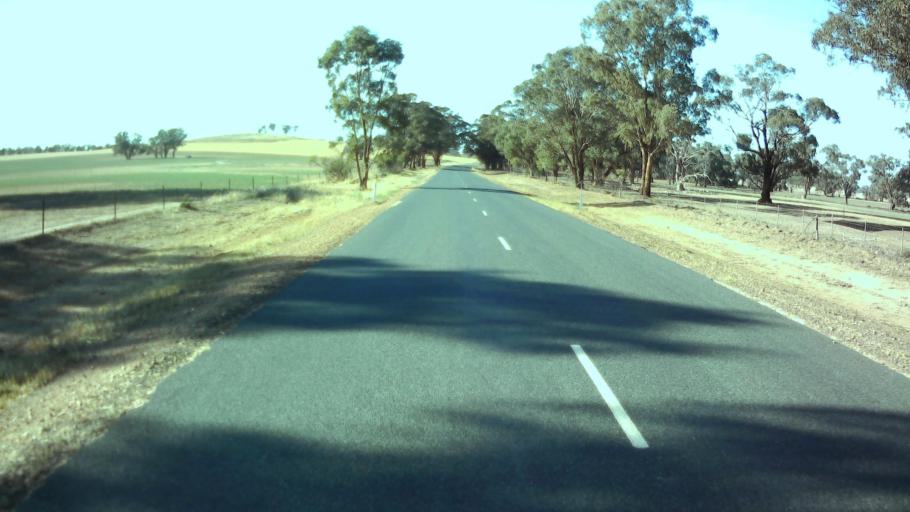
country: AU
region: New South Wales
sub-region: Weddin
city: Grenfell
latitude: -33.9646
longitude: 148.1404
